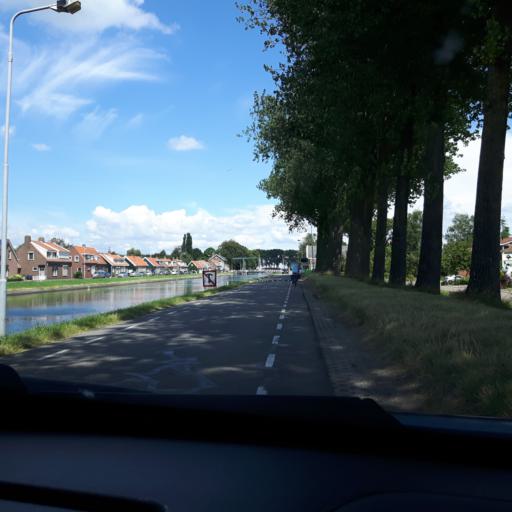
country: NL
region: Zeeland
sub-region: Gemeente Goes
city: Goes
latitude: 51.5271
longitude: 3.8978
